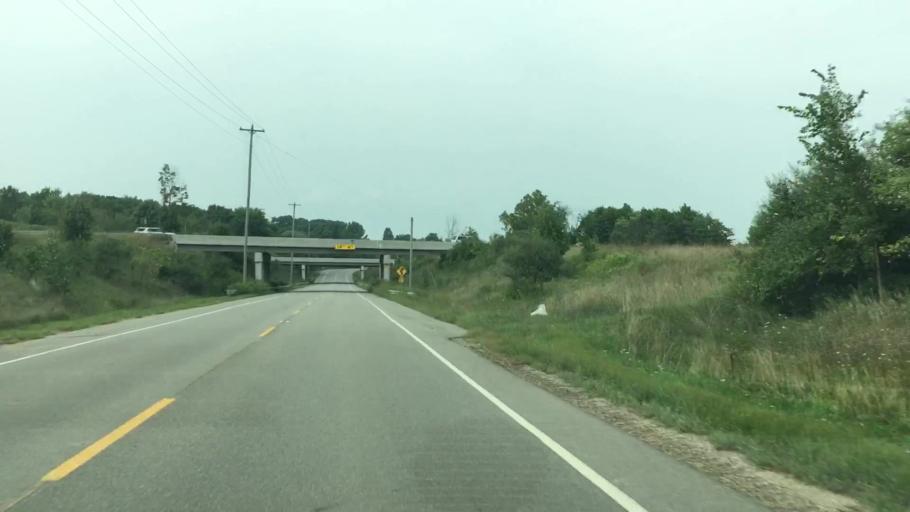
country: US
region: Michigan
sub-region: Ottawa County
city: Hudsonville
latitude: 42.8343
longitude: -85.9006
